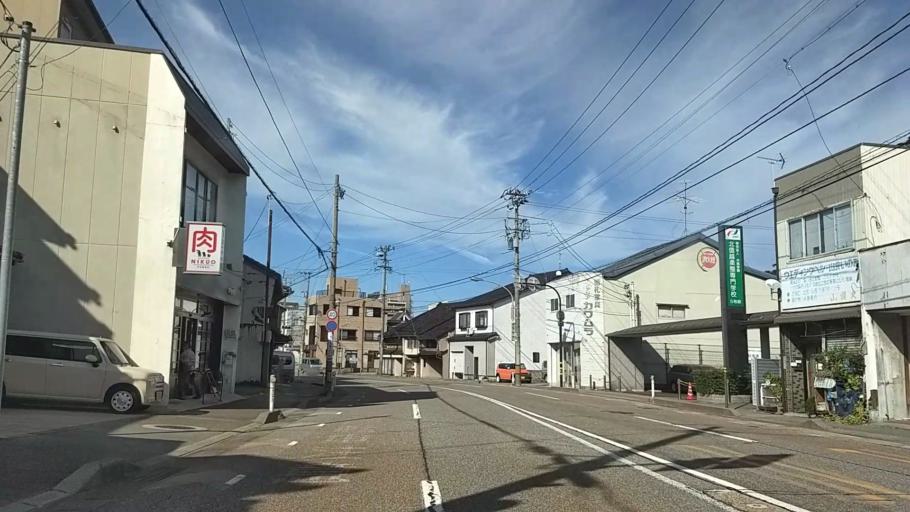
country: JP
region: Ishikawa
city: Kanazawa-shi
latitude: 36.5786
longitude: 136.6699
